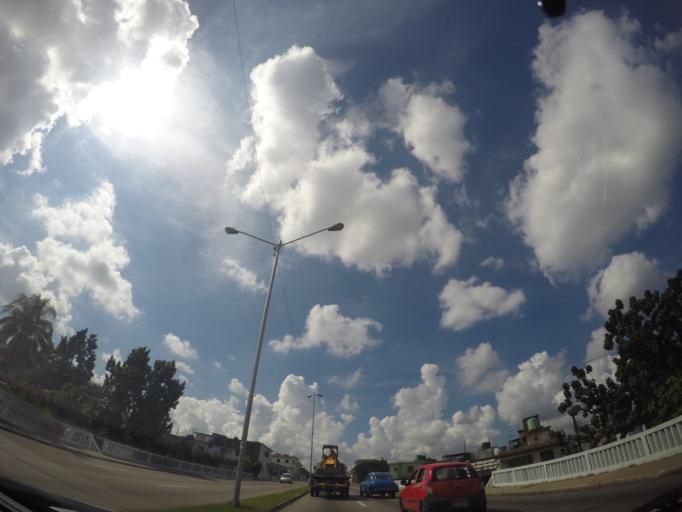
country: CU
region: La Habana
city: Cerro
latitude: 23.1009
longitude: -82.4206
